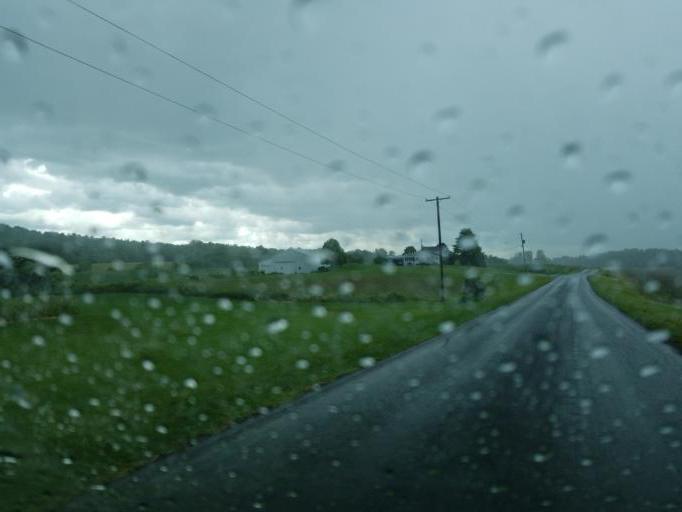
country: US
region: New York
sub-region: Wayne County
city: Clyde
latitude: 43.0339
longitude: -76.8832
